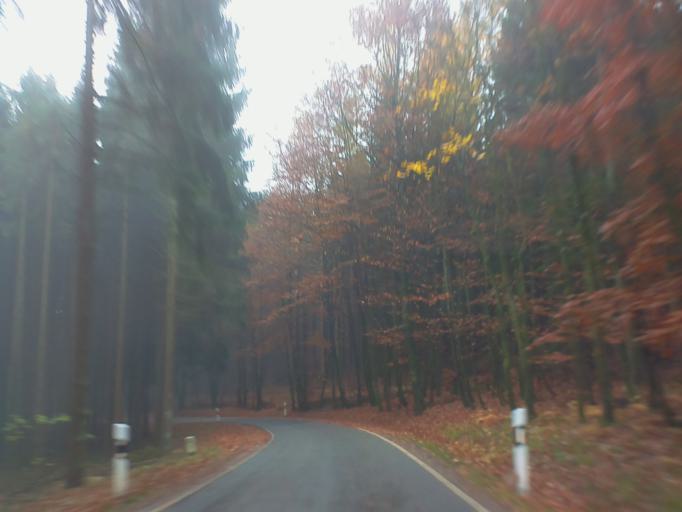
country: DE
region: Hesse
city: Neckarsteinach
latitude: 49.4331
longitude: 8.8523
